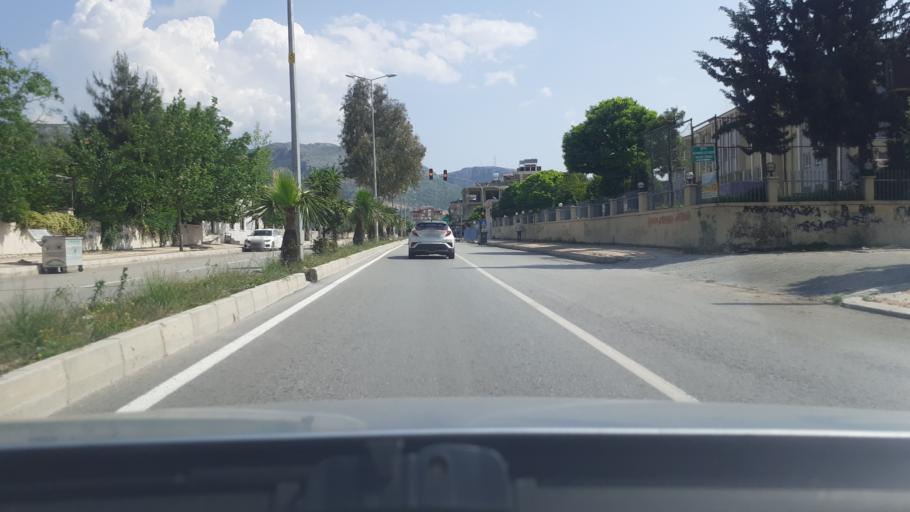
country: TR
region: Hatay
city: Harbiye
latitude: 36.1410
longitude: 36.1417
